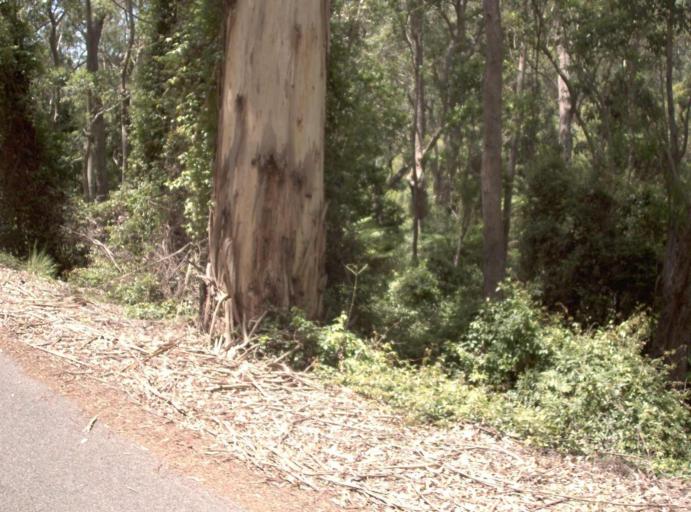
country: AU
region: New South Wales
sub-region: Bombala
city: Bombala
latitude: -37.4506
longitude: 148.9347
